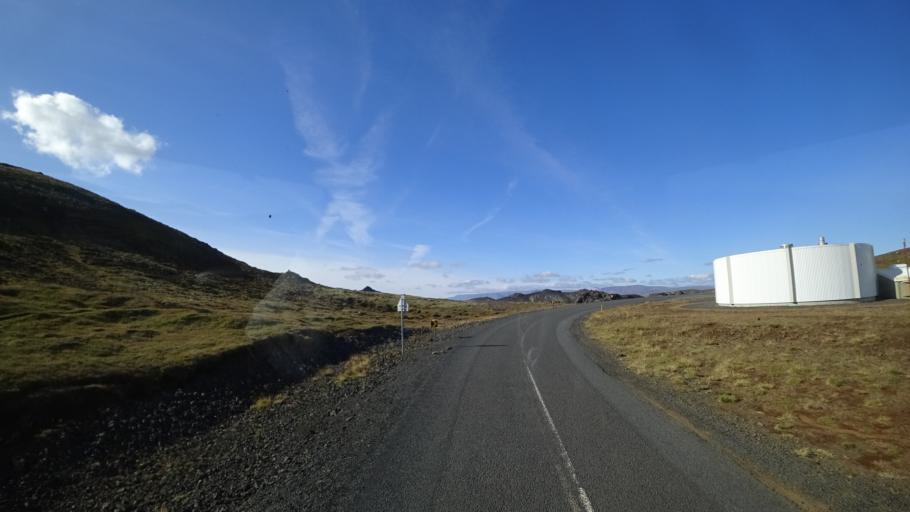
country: IS
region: South
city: Hveragerdi
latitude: 64.1095
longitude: -21.2848
